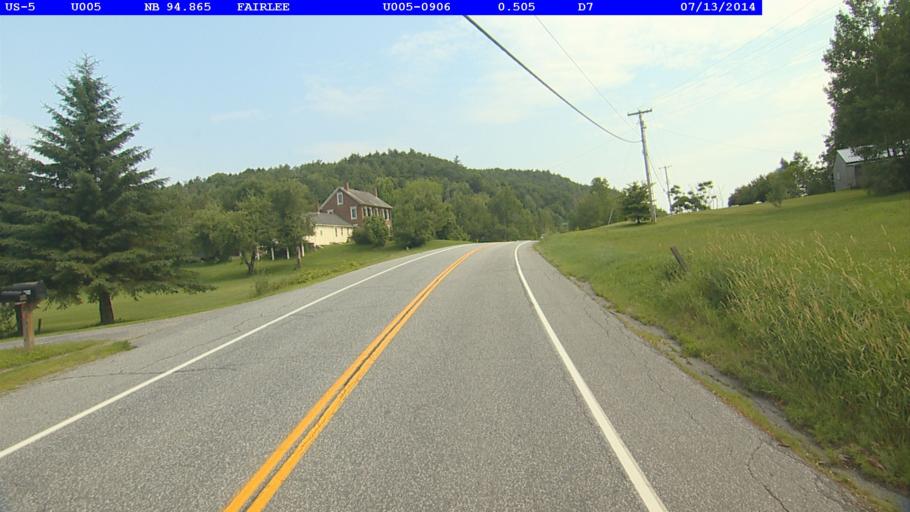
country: US
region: New Hampshire
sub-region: Grafton County
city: Orford
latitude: 43.8814
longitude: -72.1773
